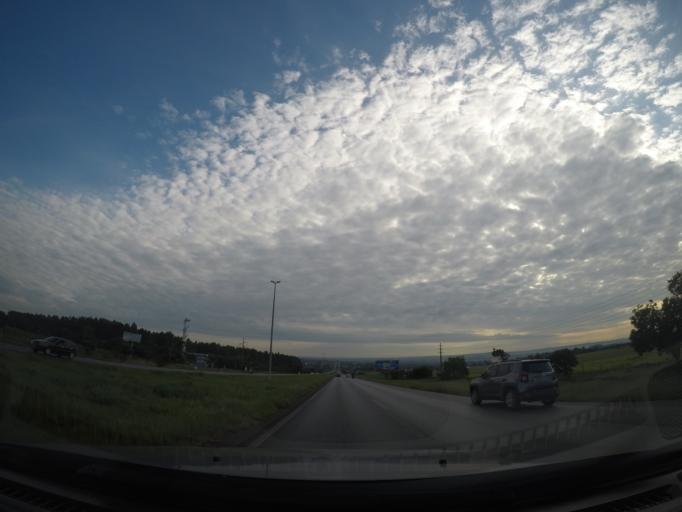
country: BR
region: Goias
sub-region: Planaltina
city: Planaltina
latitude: -15.6151
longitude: -47.7058
